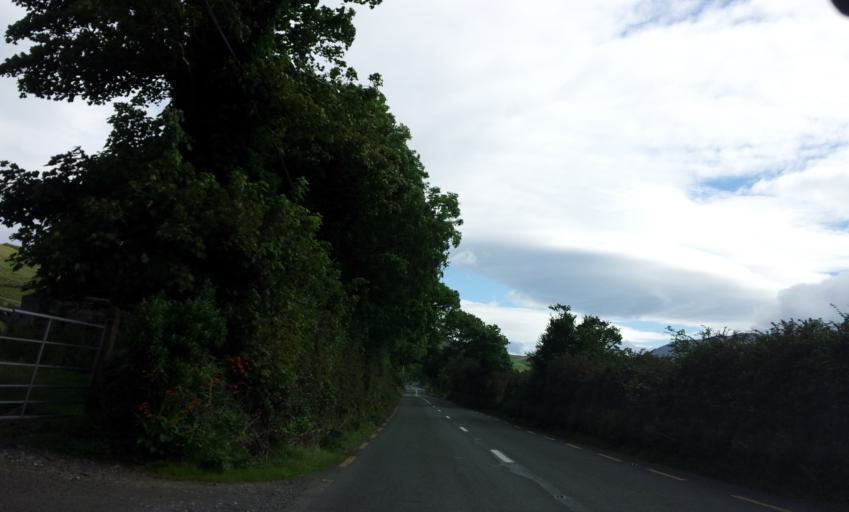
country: IE
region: Munster
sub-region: Ciarrai
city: Killorglin
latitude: 52.1873
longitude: -9.9533
